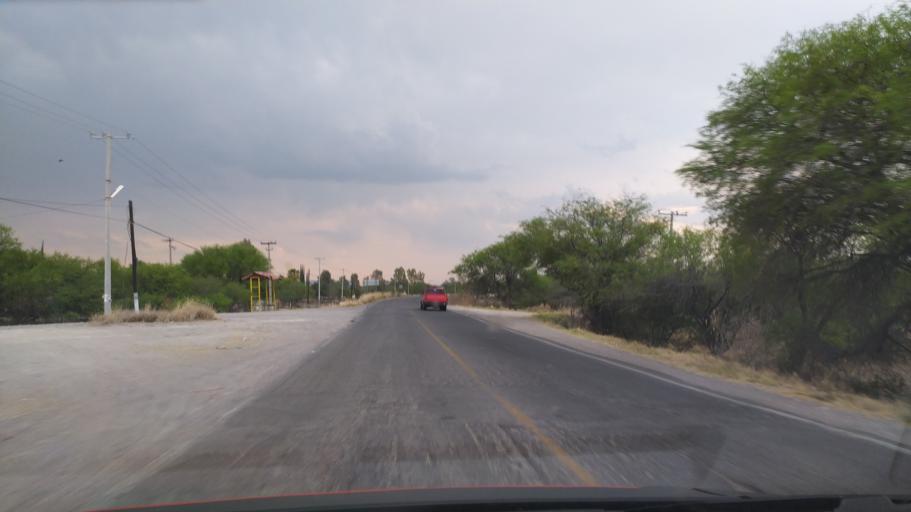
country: MX
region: Guanajuato
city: Ciudad Manuel Doblado
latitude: 20.8091
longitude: -101.9047
